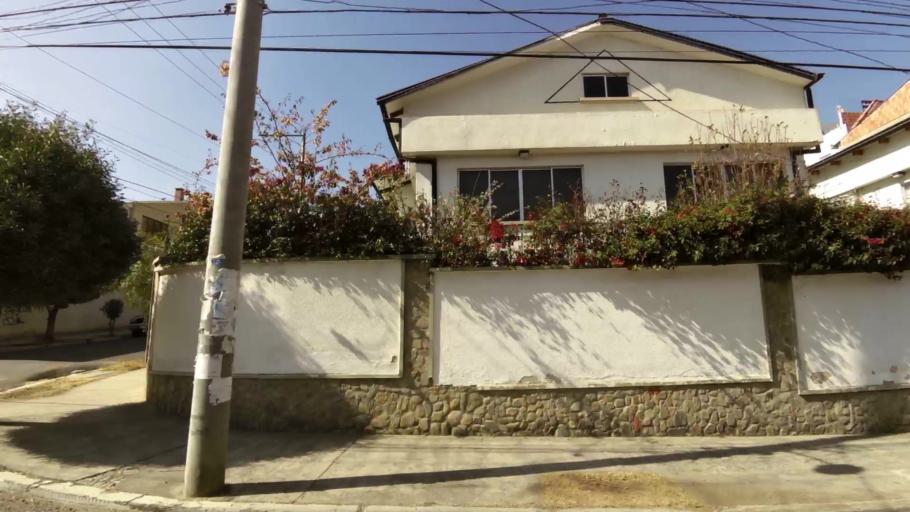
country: BO
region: La Paz
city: La Paz
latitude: -16.5328
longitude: -68.0718
